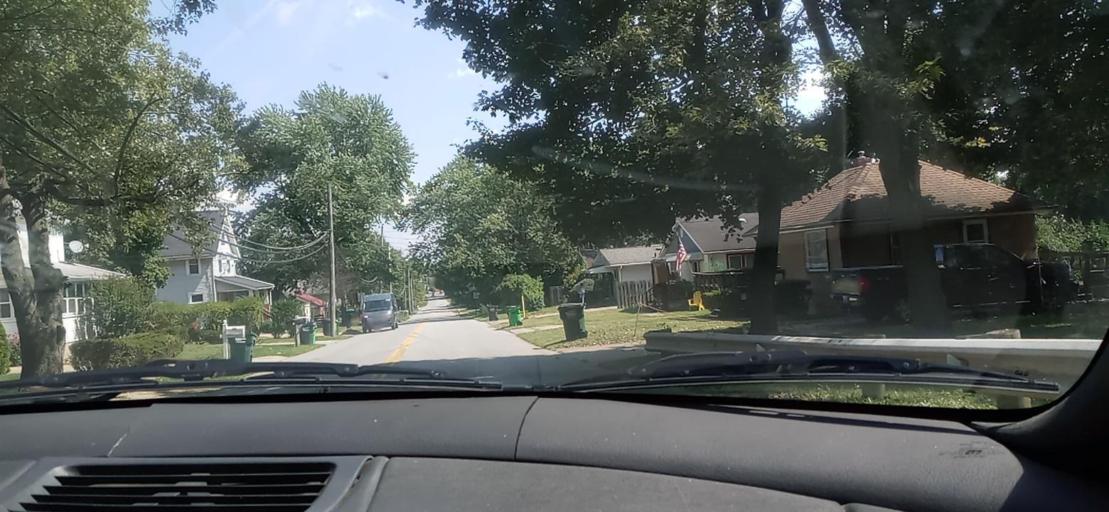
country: US
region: Ohio
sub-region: Summit County
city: Barberton
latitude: 41.0387
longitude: -81.5813
